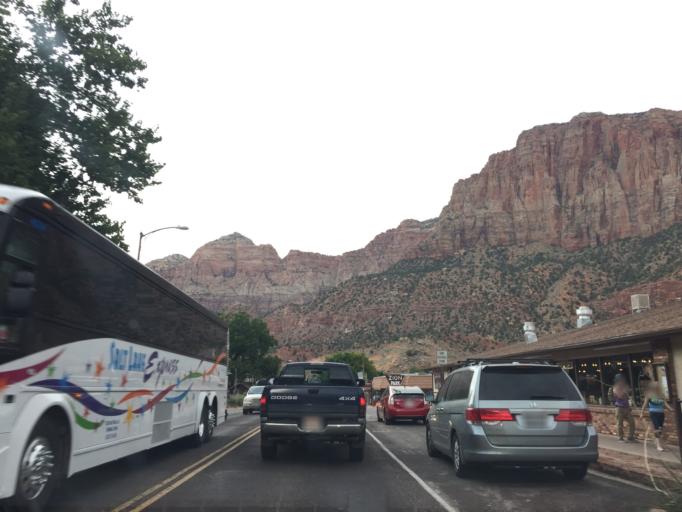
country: US
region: Utah
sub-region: Washington County
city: Hildale
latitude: 37.1888
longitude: -112.9991
